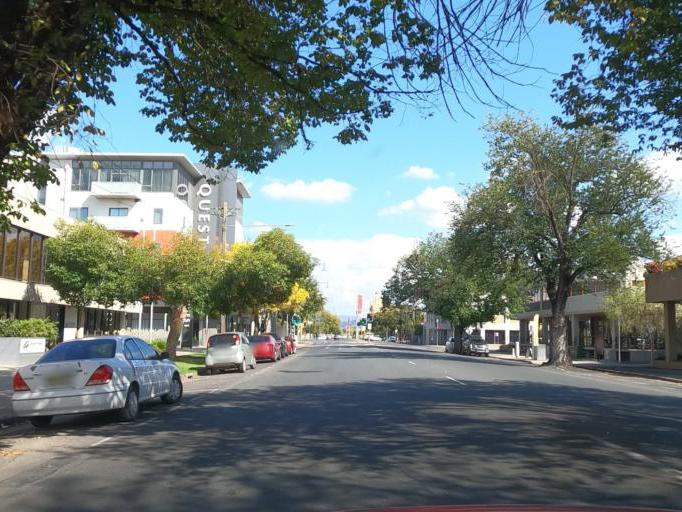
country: AU
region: New South Wales
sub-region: Albury Municipality
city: Albury
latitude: -36.0774
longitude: 146.9163
